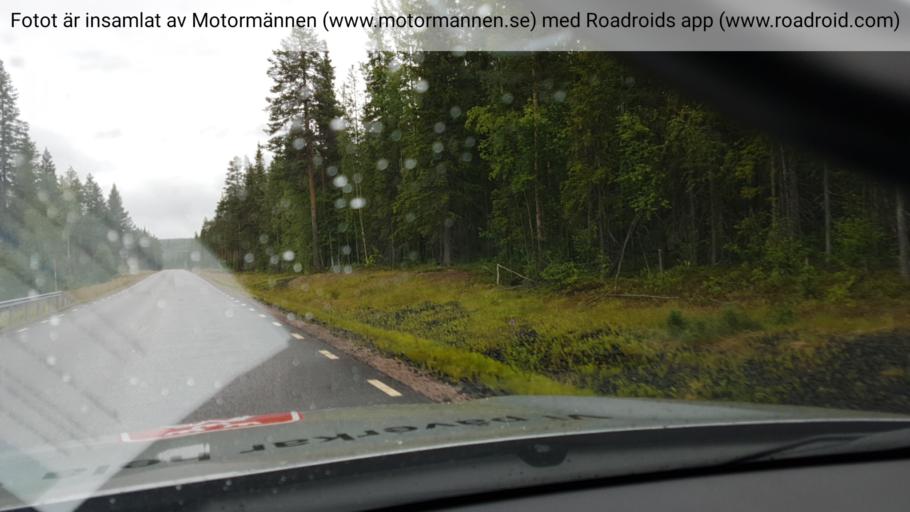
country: SE
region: Norrbotten
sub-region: Gallivare Kommun
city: Gaellivare
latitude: 66.5946
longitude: 20.4691
